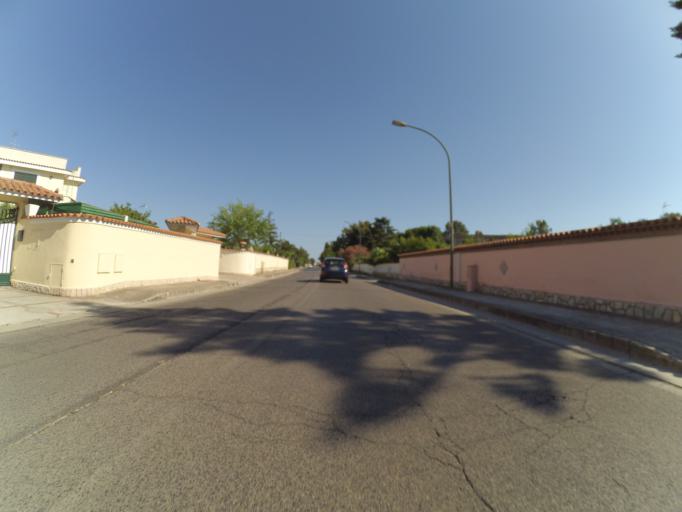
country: IT
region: Latium
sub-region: Provincia di Latina
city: San Felice Circeo
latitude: 41.2582
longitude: 13.0915
